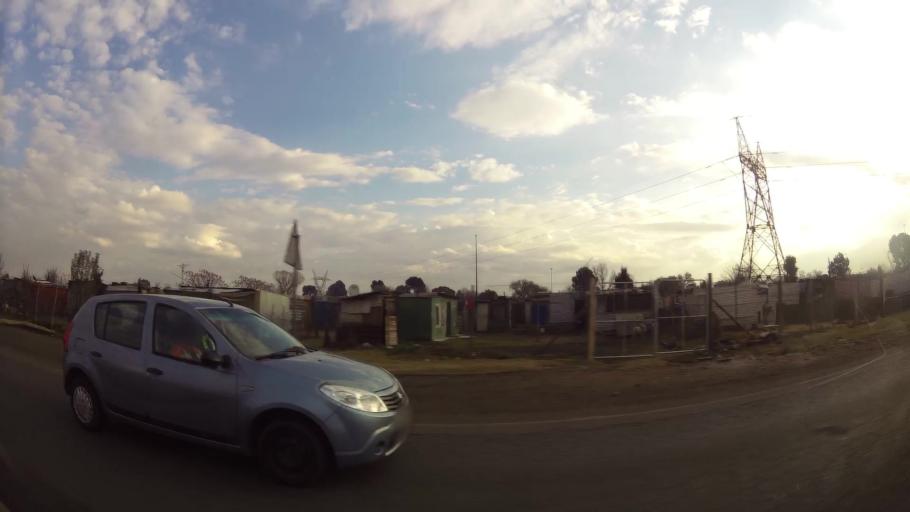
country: ZA
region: Gauteng
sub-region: Sedibeng District Municipality
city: Vanderbijlpark
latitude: -26.6927
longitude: 27.8049
